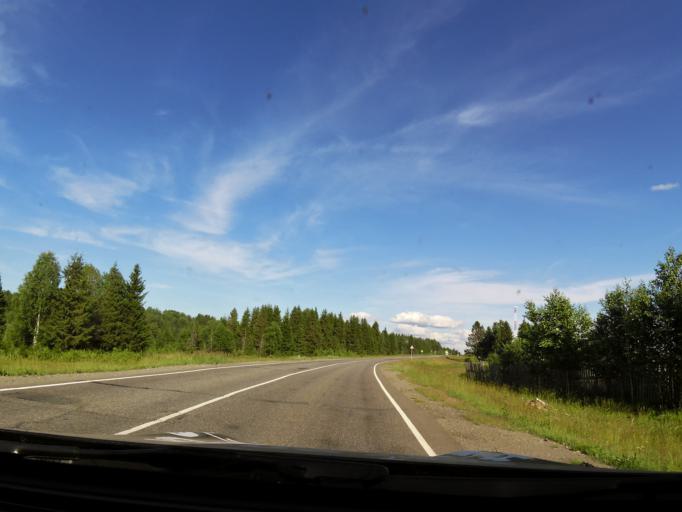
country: RU
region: Kirov
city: Chernaya Kholunitsa
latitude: 58.8579
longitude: 51.7165
